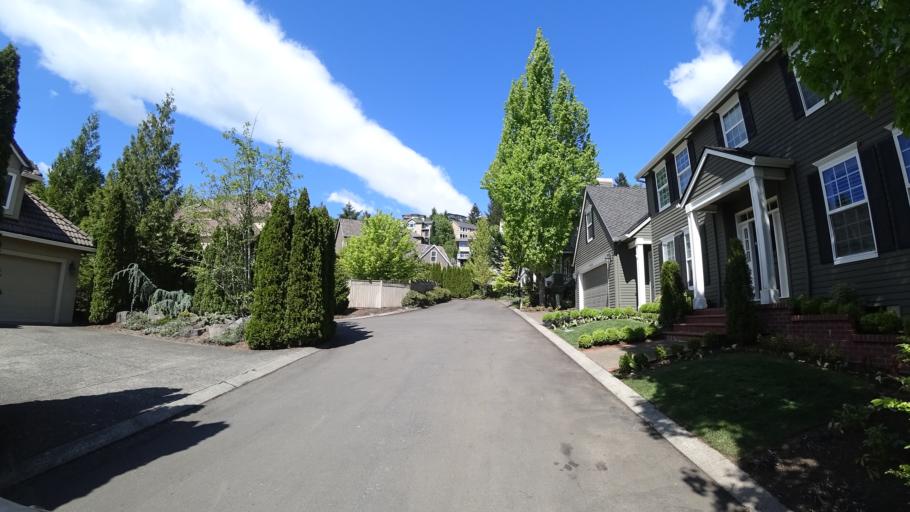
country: US
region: Oregon
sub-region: Washington County
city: West Haven
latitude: 45.5472
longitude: -122.7762
